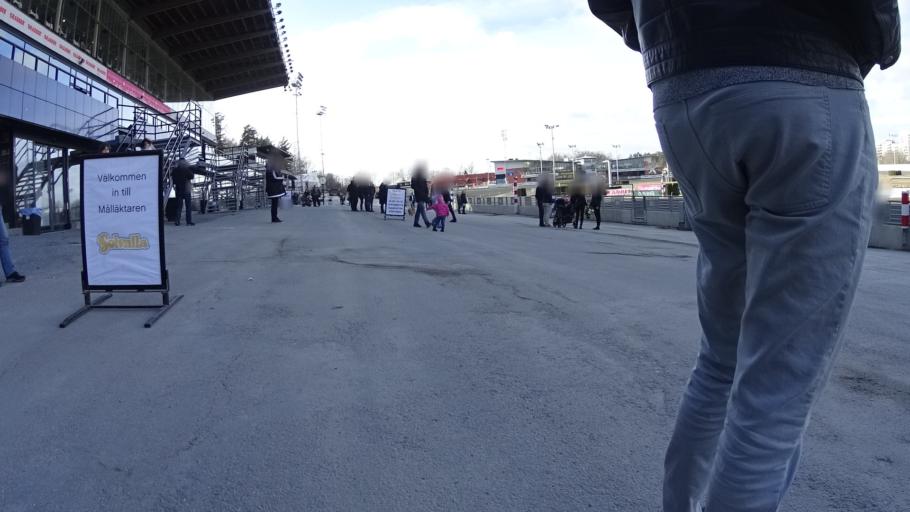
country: SE
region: Stockholm
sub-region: Stockholms Kommun
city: Bromma
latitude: 59.3665
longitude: 17.9393
